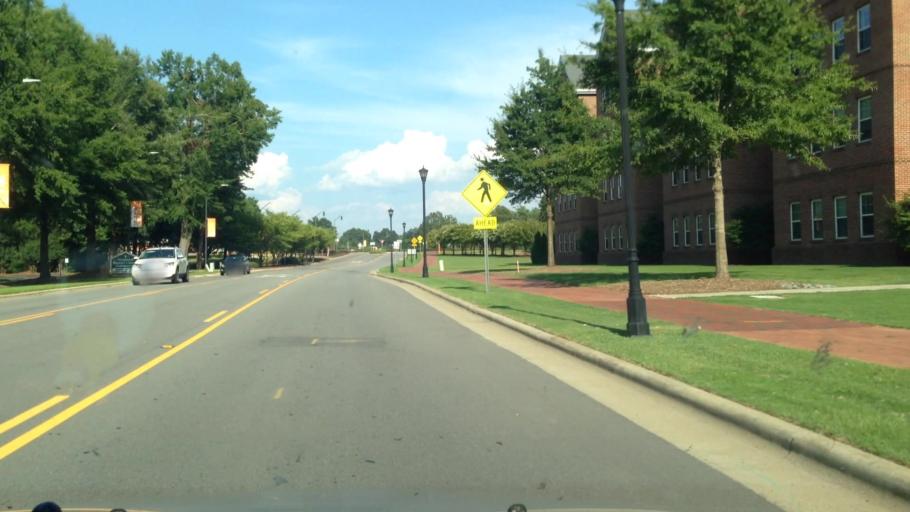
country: US
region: North Carolina
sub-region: Harnett County
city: Buies Creek
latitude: 35.4073
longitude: -78.7430
